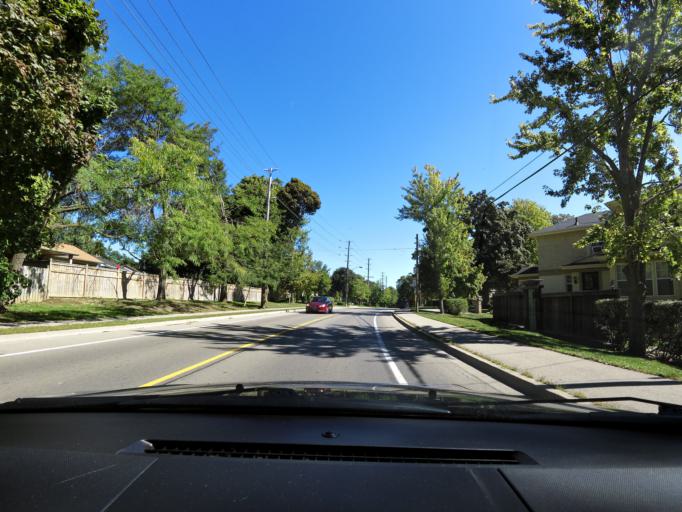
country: CA
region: Ontario
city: Hamilton
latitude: 43.3145
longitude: -79.8121
